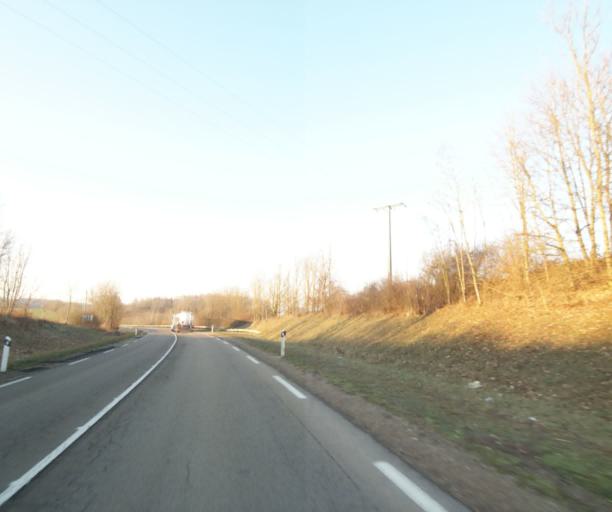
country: FR
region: Champagne-Ardenne
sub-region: Departement de la Haute-Marne
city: Bienville
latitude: 48.5772
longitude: 5.0348
